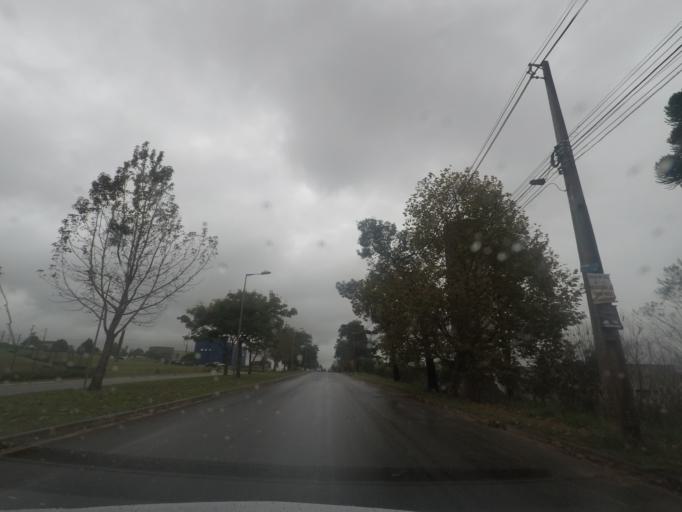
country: BR
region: Parana
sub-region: Pinhais
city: Pinhais
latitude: -25.3915
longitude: -49.1601
